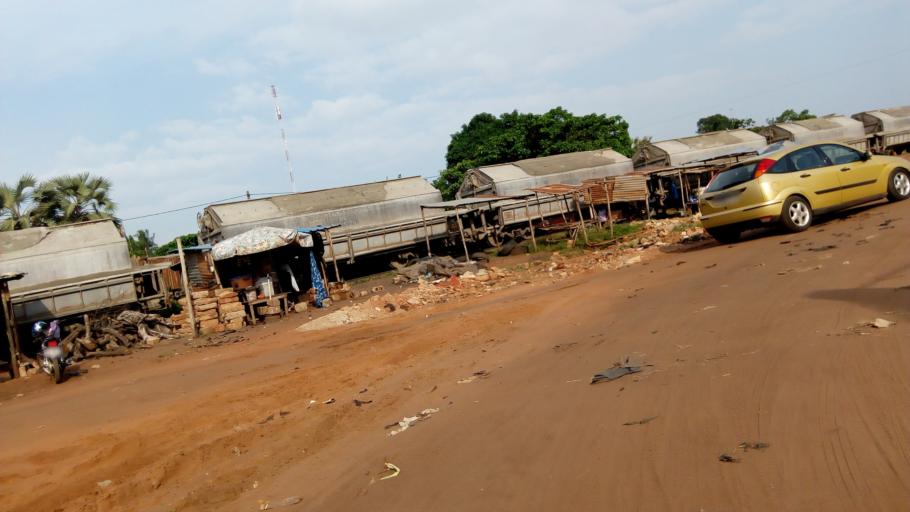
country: TG
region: Maritime
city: Lome
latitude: 6.2151
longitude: 1.2066
